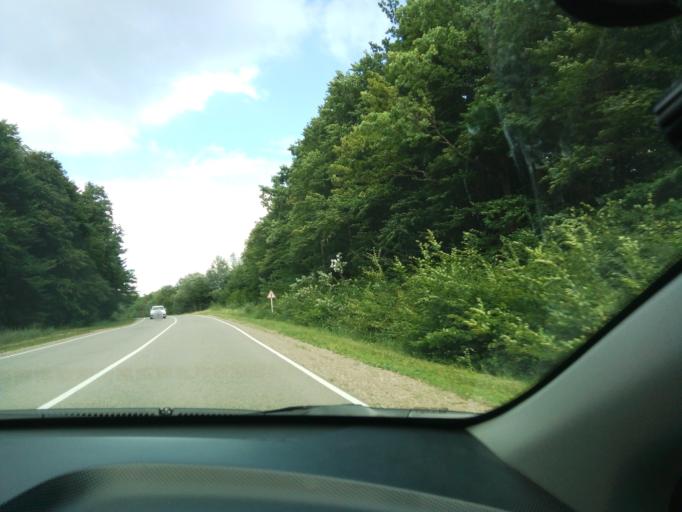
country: RU
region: Krasnodarskiy
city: Apsheronsk
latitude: 44.4800
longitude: 39.9294
